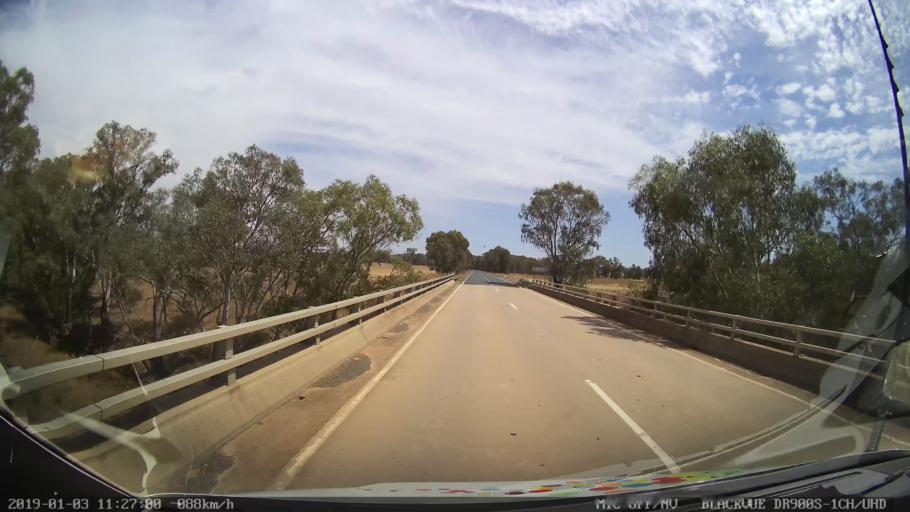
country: AU
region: New South Wales
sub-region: Weddin
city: Grenfell
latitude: -34.0175
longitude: 148.2214
